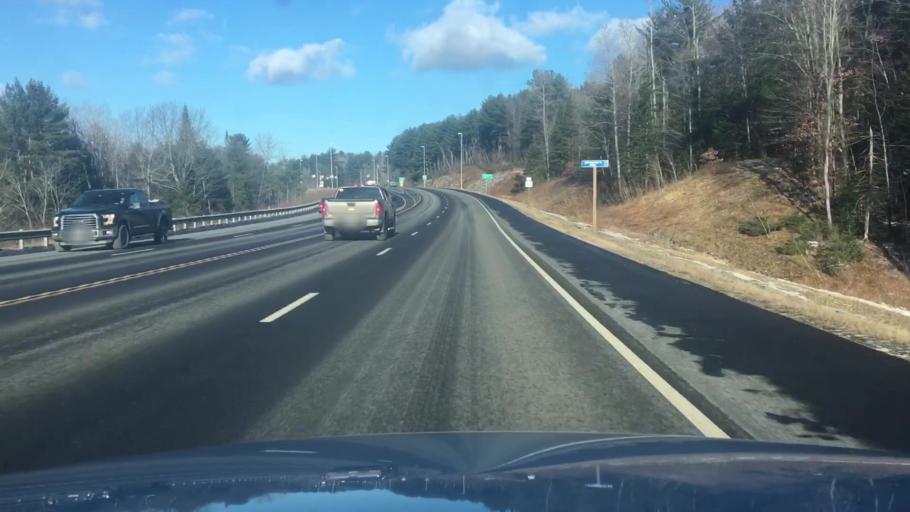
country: US
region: Maine
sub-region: Kennebec County
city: Augusta
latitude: 44.3427
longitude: -69.7687
